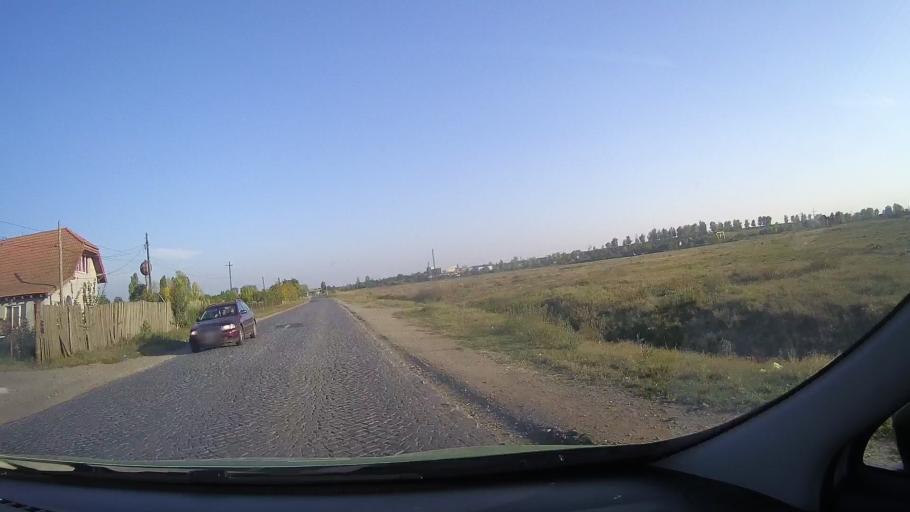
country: RO
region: Bihor
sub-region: Comuna Bors
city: Santion
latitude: 47.1064
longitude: 21.8706
